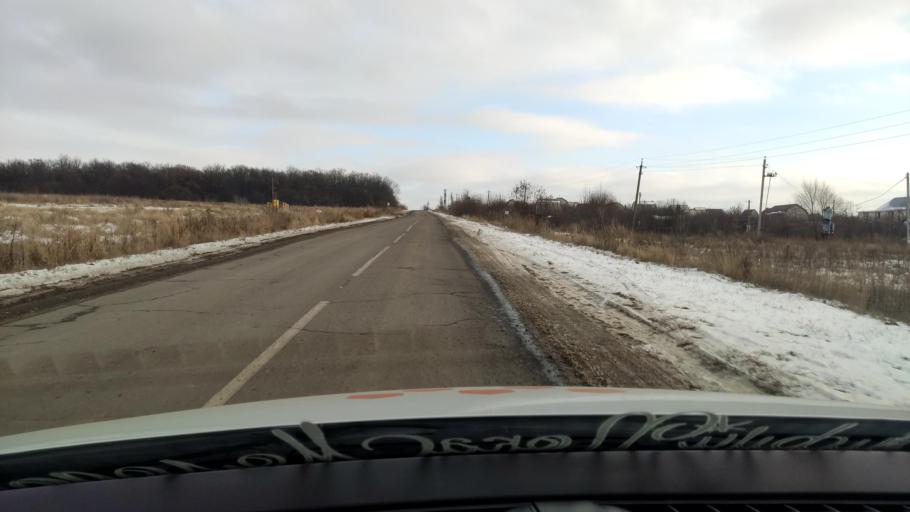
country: RU
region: Voronezj
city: Semiluki
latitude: 51.7499
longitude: 39.0339
